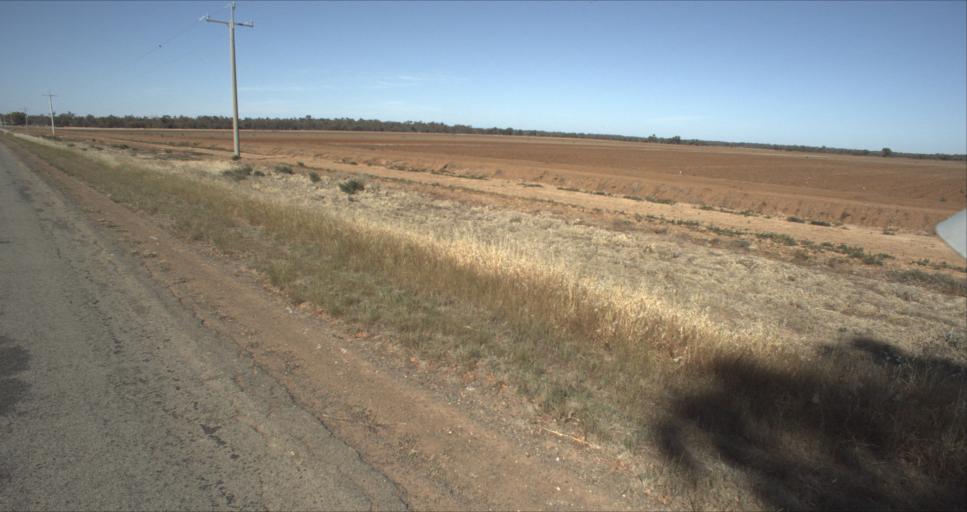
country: AU
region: New South Wales
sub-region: Leeton
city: Leeton
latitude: -34.5987
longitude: 146.2581
